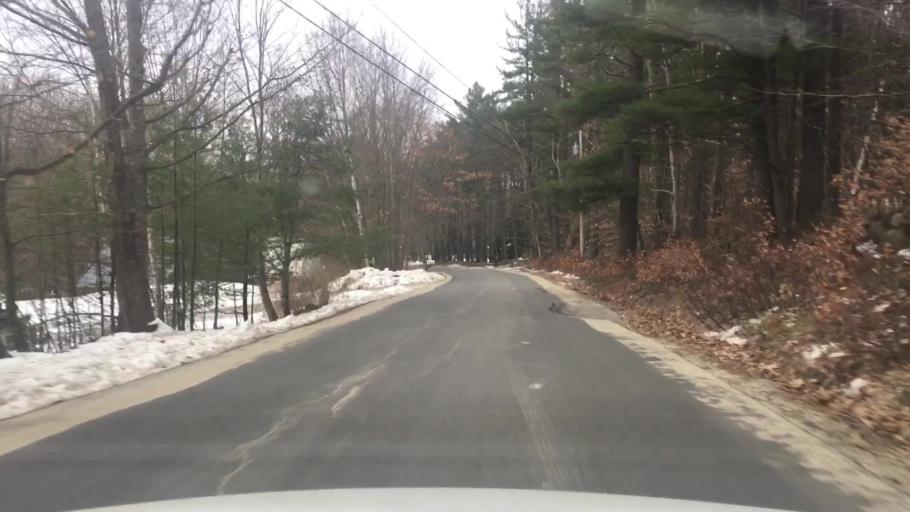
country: US
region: New Hampshire
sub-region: Merrimack County
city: Hopkinton
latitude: 43.1782
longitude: -71.6748
